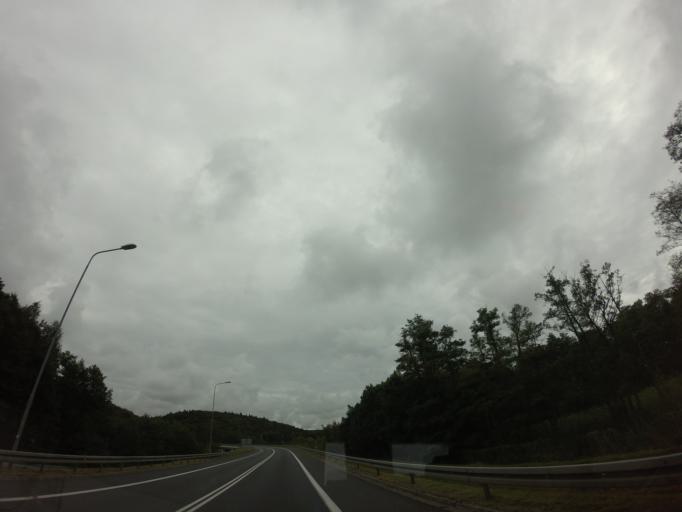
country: PL
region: West Pomeranian Voivodeship
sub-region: Powiat kamienski
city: Miedzyzdroje
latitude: 53.9092
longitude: 14.4322
